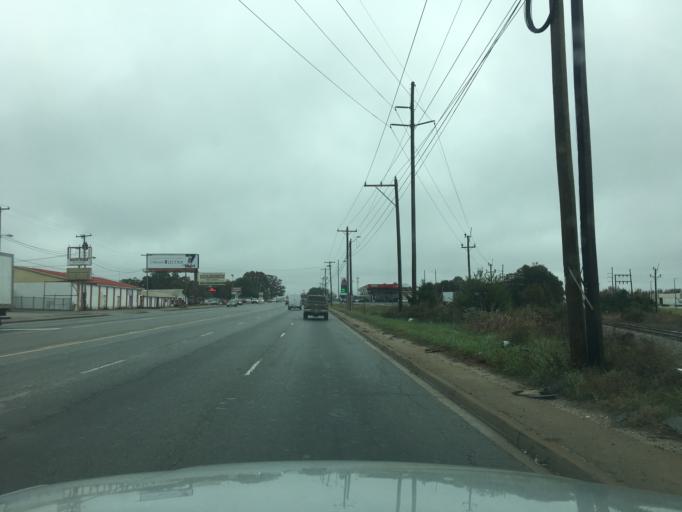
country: US
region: South Carolina
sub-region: Greenville County
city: Gantt
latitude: 34.8052
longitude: -82.4322
